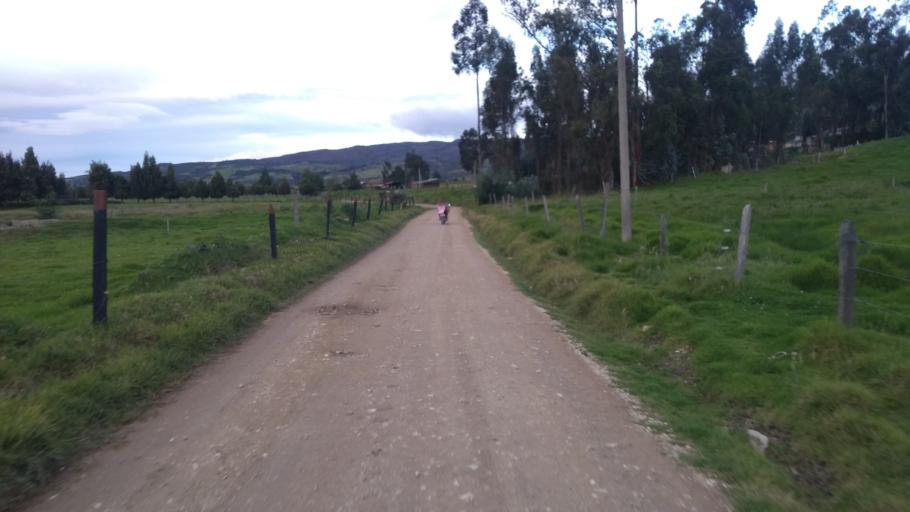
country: CO
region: Boyaca
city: Toca
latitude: 5.6211
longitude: -73.1611
